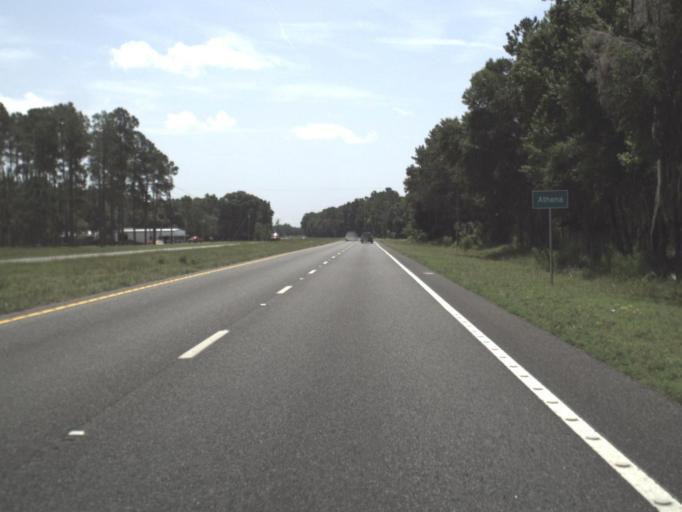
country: US
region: Florida
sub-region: Taylor County
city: Perry
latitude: 29.9870
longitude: -83.4958
